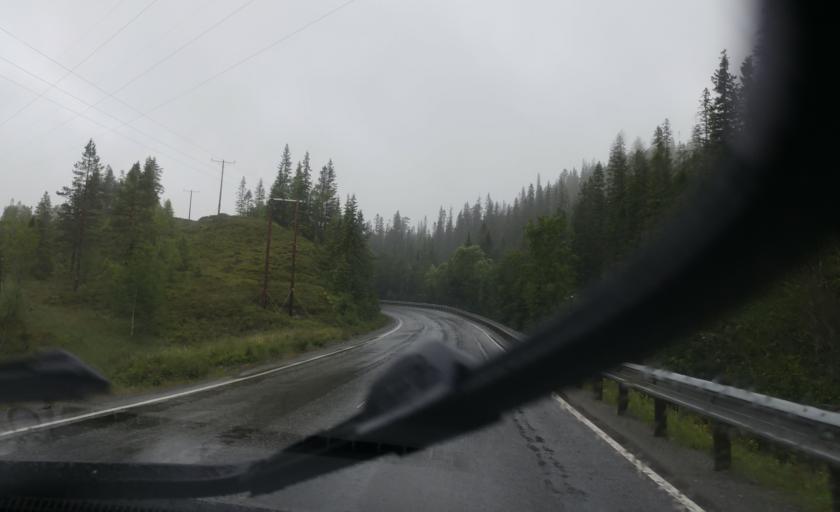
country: NO
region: Sor-Trondelag
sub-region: Selbu
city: Mebonden
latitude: 63.3553
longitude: 11.0756
